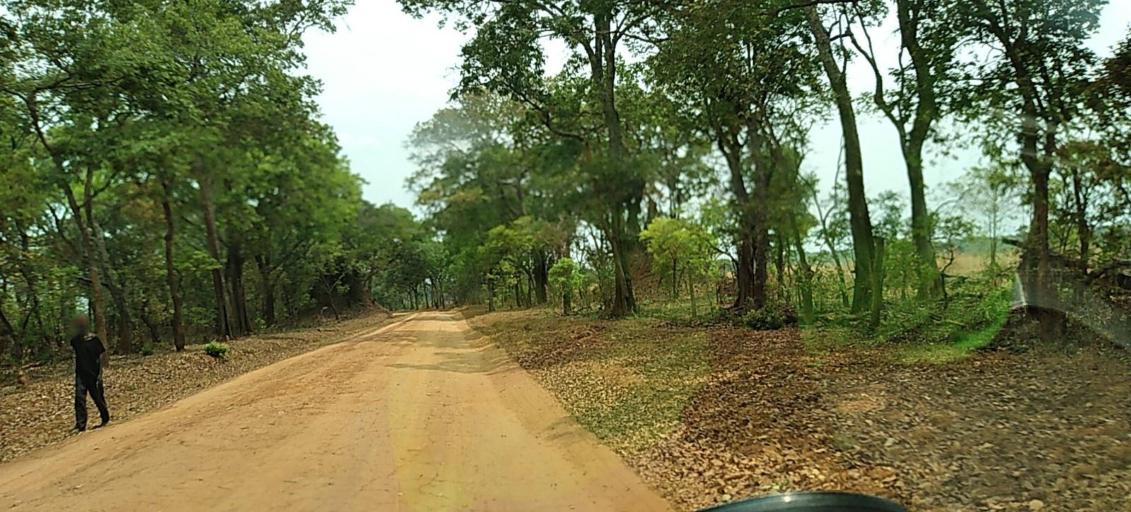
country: ZM
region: North-Western
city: Solwezi
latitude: -12.8148
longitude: 26.5363
